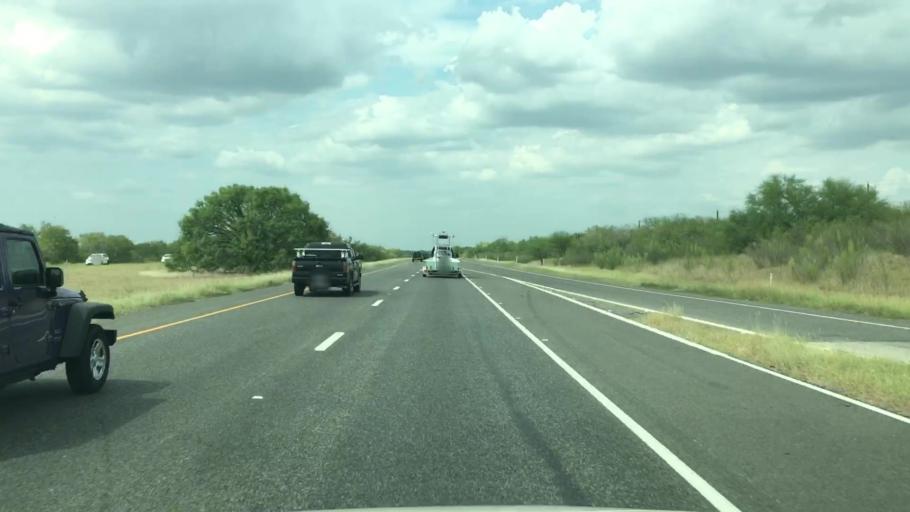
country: US
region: Texas
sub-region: Atascosa County
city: Pleasanton
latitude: 28.9189
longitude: -98.4347
